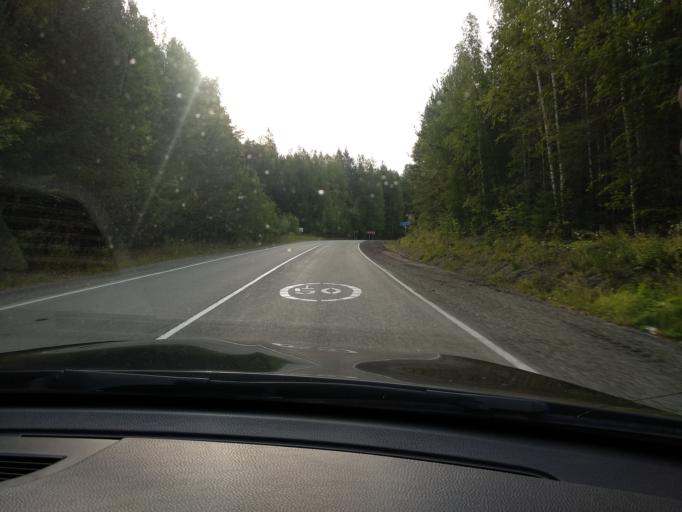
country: RU
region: Sverdlovsk
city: Rudnichnyy
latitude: 59.6746
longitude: 60.3386
